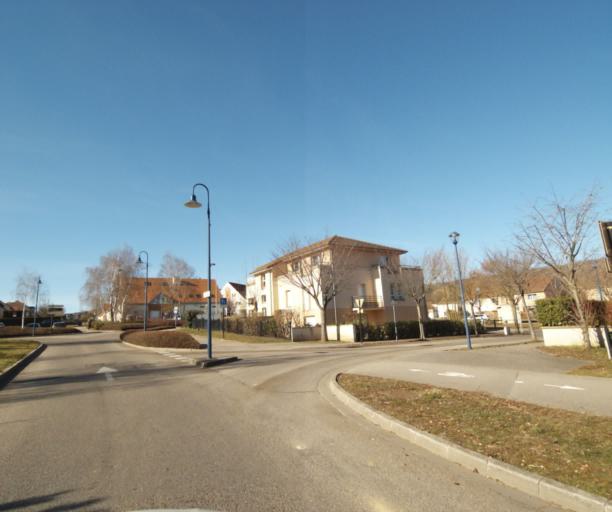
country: FR
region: Lorraine
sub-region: Departement de Meurthe-et-Moselle
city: Ludres
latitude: 48.6200
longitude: 6.1711
